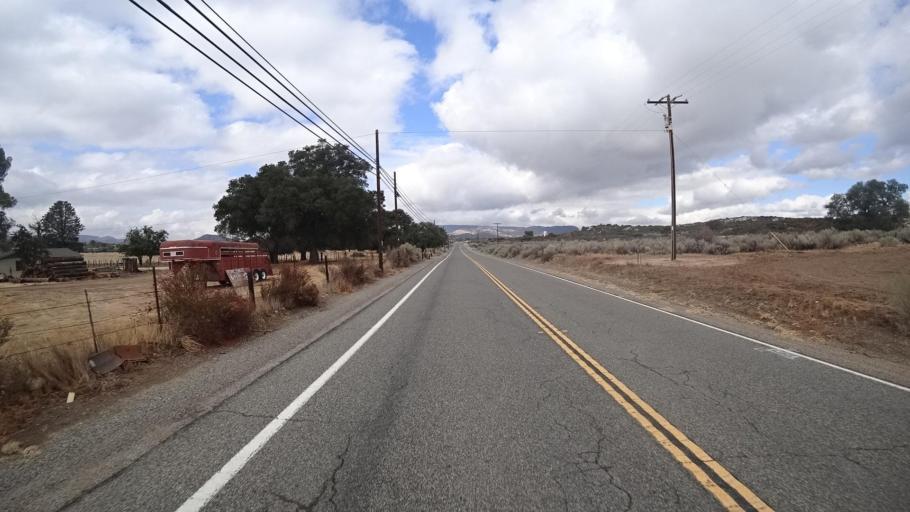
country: US
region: California
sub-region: San Diego County
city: Campo
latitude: 32.6302
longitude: -116.4542
